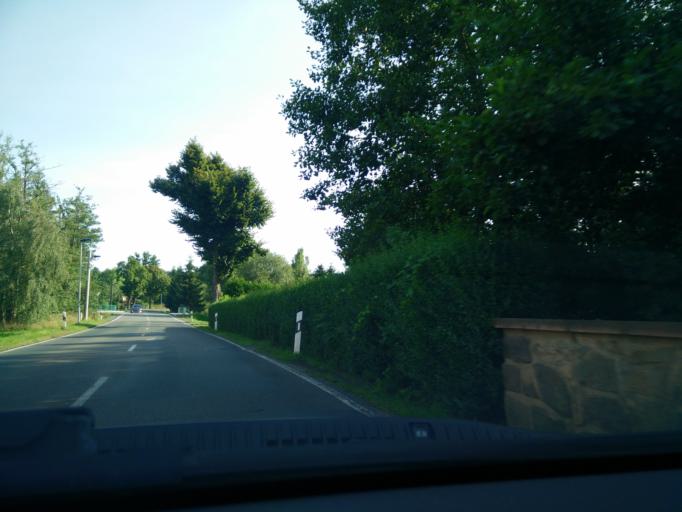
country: DE
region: Saxony
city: Bad Lausick
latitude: 51.1385
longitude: 12.6506
